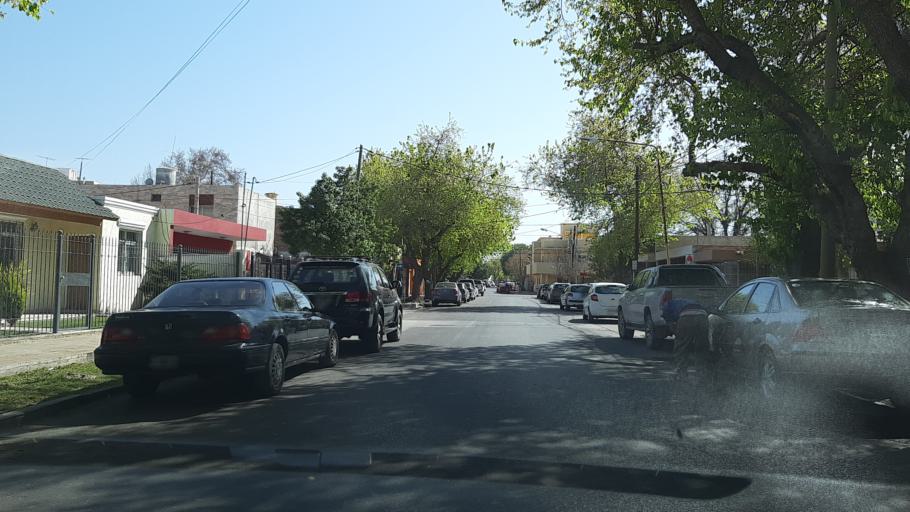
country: AR
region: San Juan
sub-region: Departamento de Santa Lucia
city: Santa Lucia
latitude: -31.5364
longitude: -68.5118
